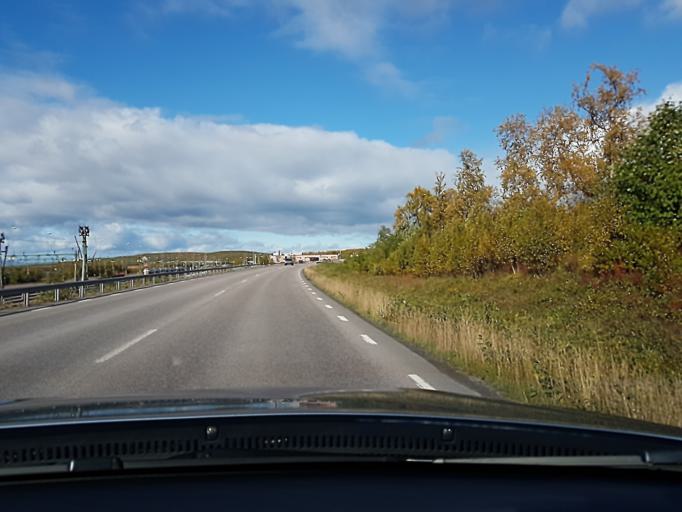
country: SE
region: Norrbotten
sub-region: Kiruna Kommun
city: Kiruna
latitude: 67.8649
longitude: 20.2036
